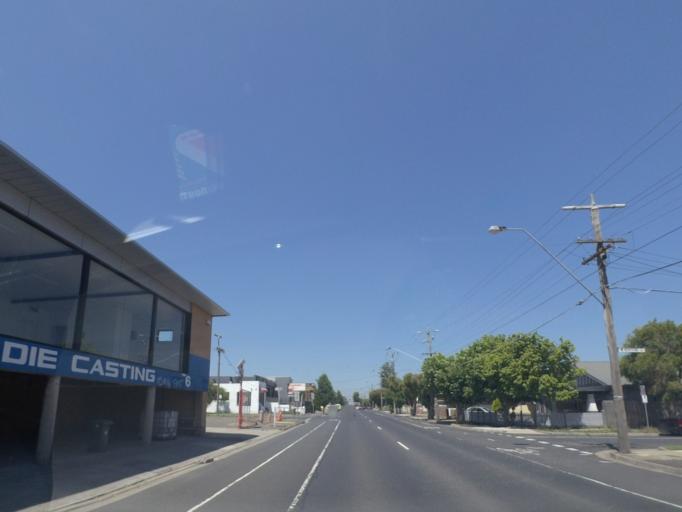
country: AU
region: Victoria
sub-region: Moreland
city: Coburg North
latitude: -37.7329
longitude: 144.9548
